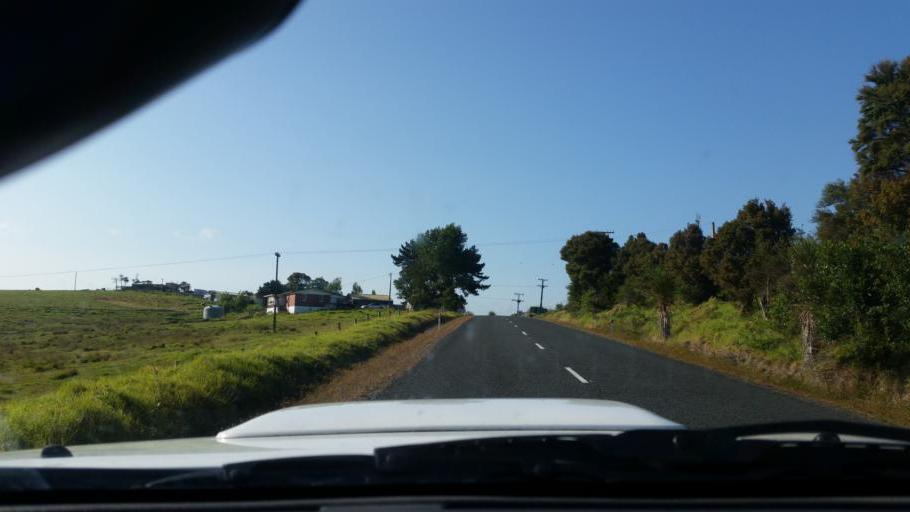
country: NZ
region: Northland
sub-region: Whangarei
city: Ruakaka
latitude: -36.1193
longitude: 174.2323
